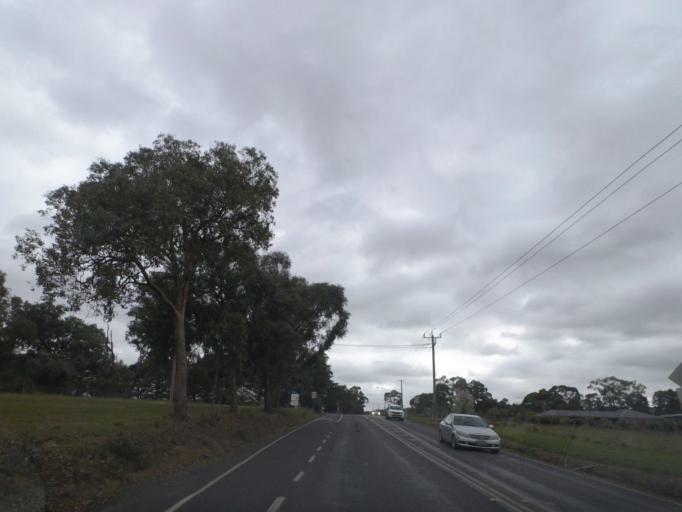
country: AU
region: Victoria
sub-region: Nillumbik
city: Doreen
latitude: -37.6273
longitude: 145.1343
